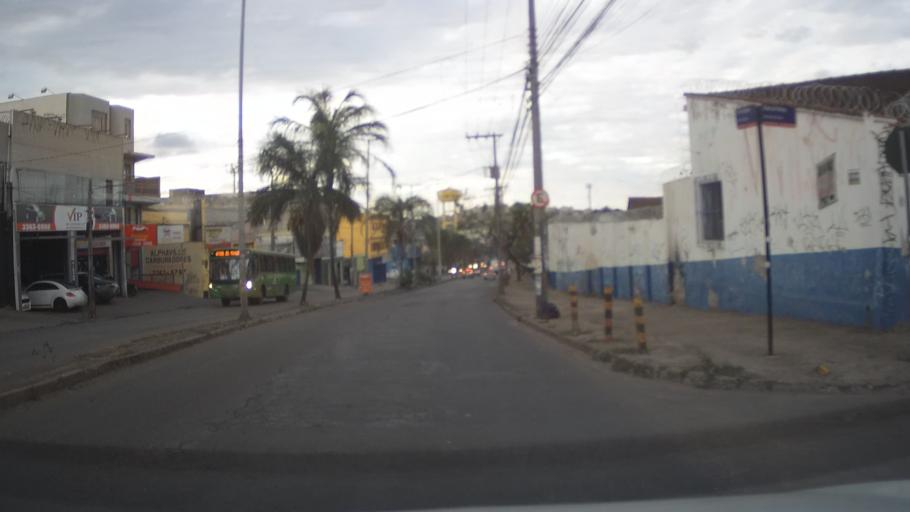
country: BR
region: Minas Gerais
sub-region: Contagem
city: Contagem
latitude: -19.9637
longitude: -44.0160
